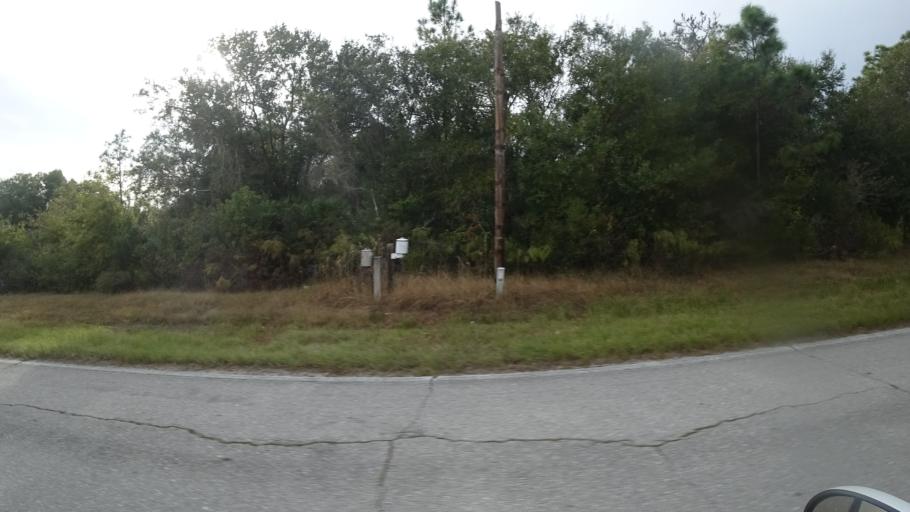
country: US
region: Florida
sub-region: Sarasota County
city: The Meadows
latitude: 27.4204
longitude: -82.2709
